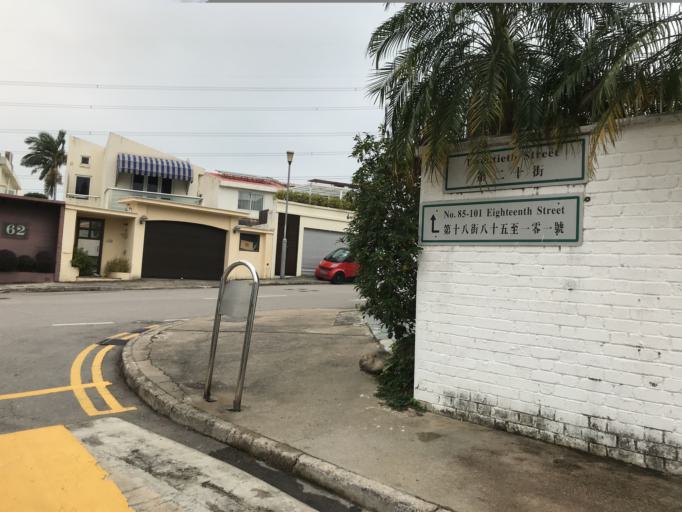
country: HK
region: Tai Po
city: Tai Po
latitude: 22.4657
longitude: 114.1546
